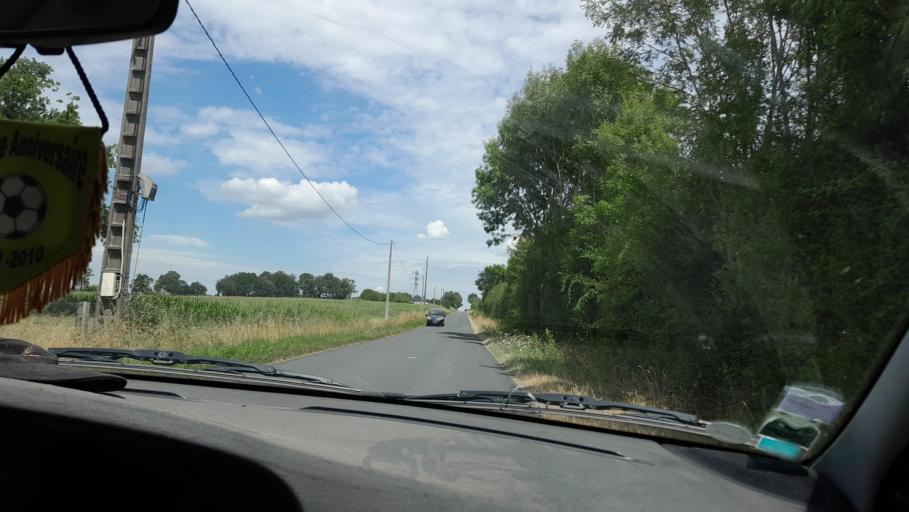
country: FR
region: Pays de la Loire
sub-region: Departement de la Mayenne
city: Saint-Pierre-la-Cour
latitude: 48.1219
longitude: -1.0253
